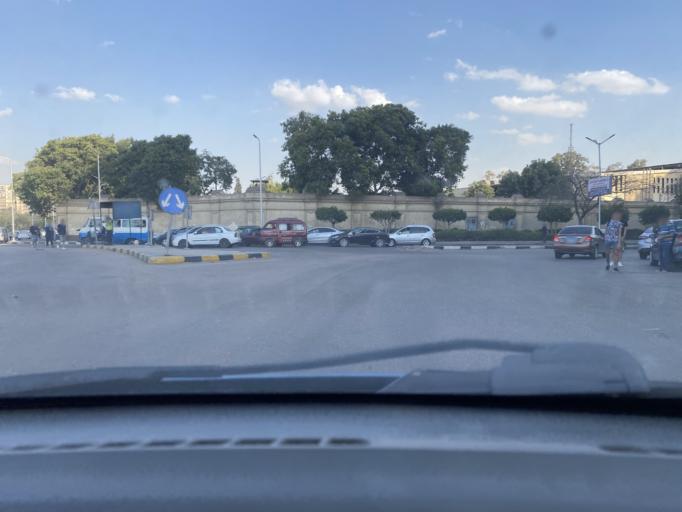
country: EG
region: Muhafazat al Qahirah
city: Cairo
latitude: 30.1028
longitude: 31.3009
